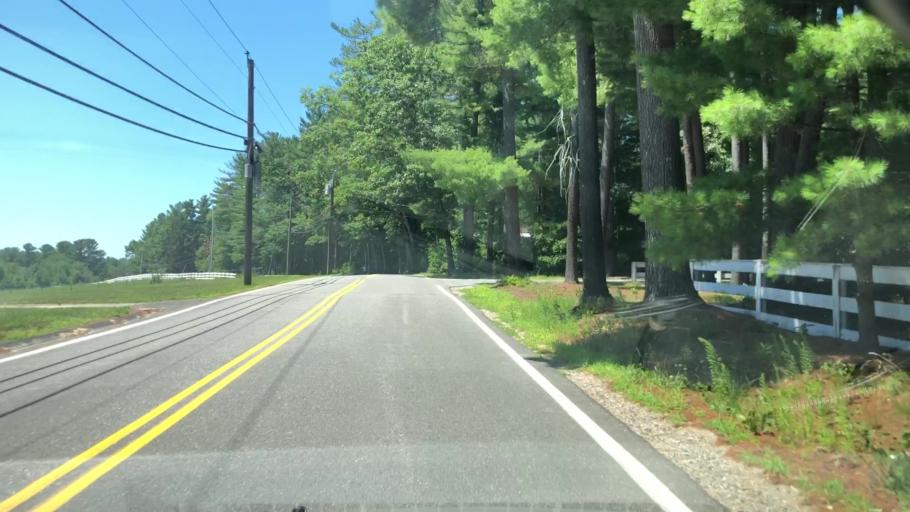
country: US
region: New Hampshire
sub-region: Hillsborough County
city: Milford
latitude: 42.8382
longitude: -71.6066
